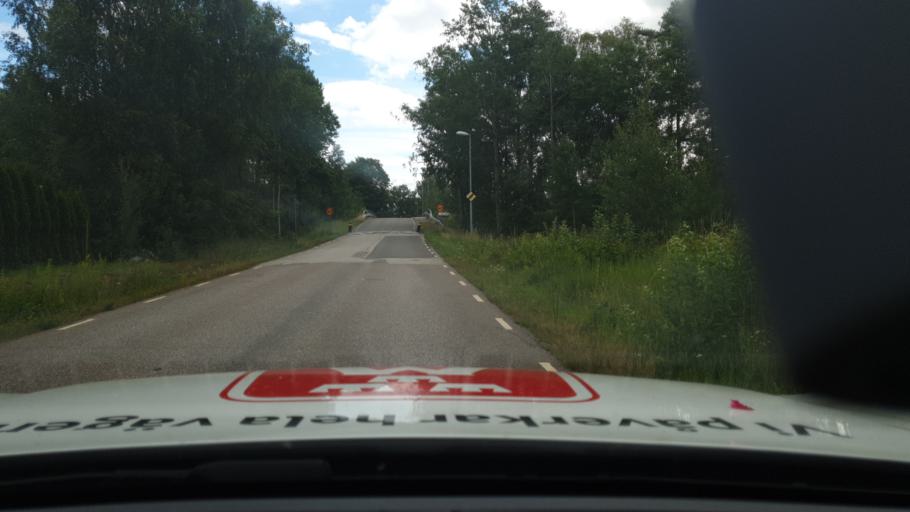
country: SE
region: Vaestra Goetaland
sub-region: Skovde Kommun
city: Skoevde
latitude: 58.4156
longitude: 13.8774
